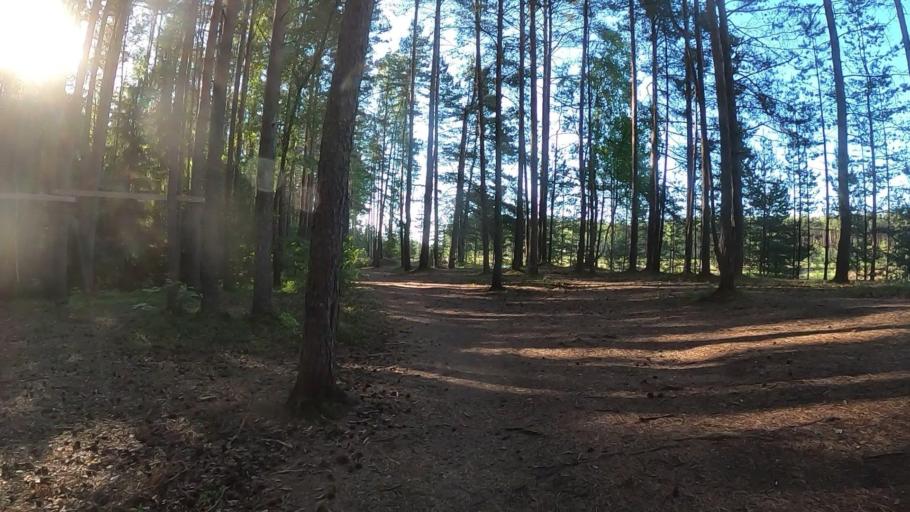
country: LV
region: Ikskile
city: Ikskile
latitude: 56.8397
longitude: 24.5498
